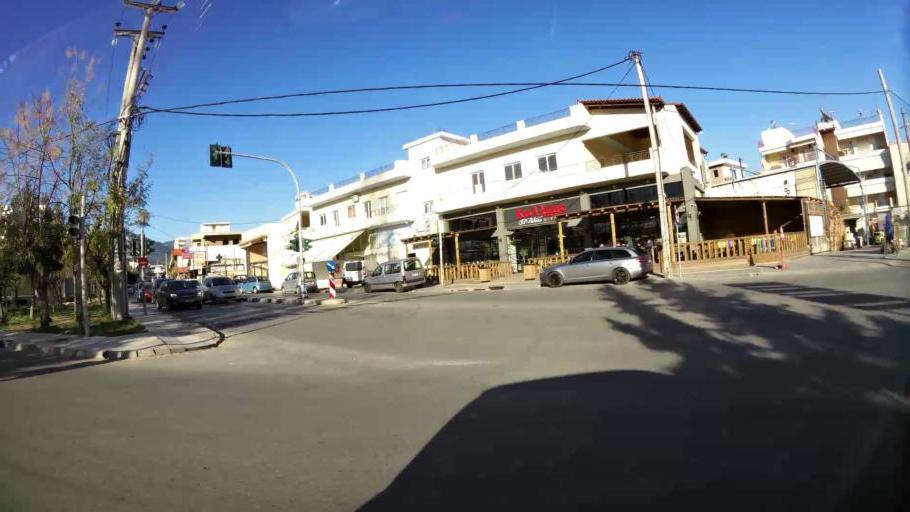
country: GR
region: Attica
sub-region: Nomarchia Anatolikis Attikis
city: Acharnes
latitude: 38.0844
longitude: 23.7258
